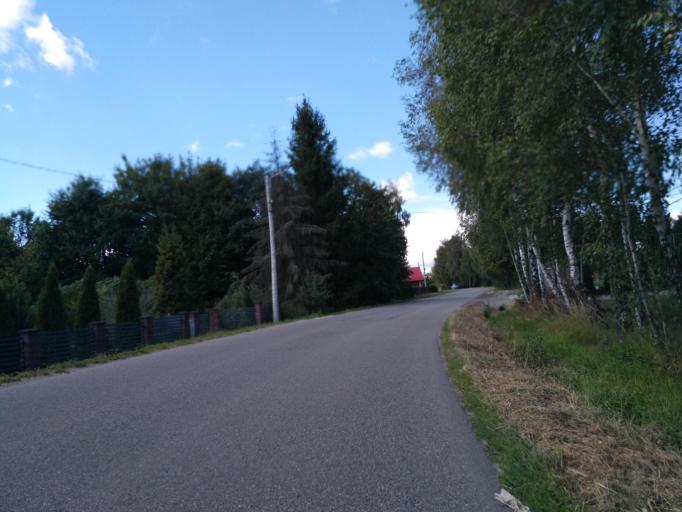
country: PL
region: Subcarpathian Voivodeship
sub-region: Powiat jasielski
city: Skolyszyn
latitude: 49.7802
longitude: 21.3672
